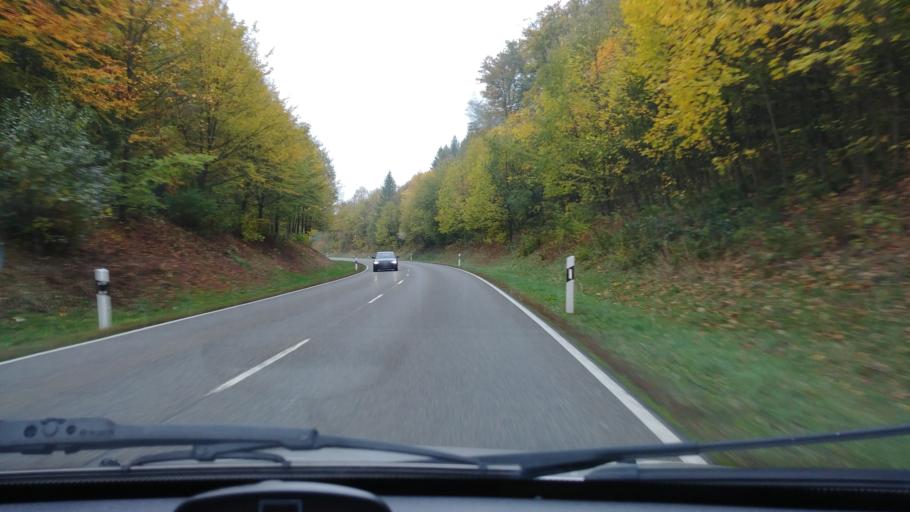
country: DE
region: Rheinland-Pfalz
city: Willmenrod
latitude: 50.5642
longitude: 7.9548
